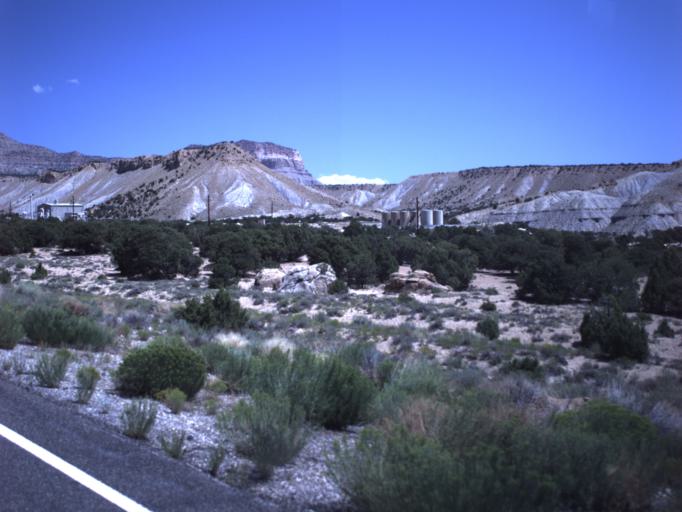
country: US
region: Utah
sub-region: Emery County
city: Orangeville
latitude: 39.2710
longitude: -111.1018
